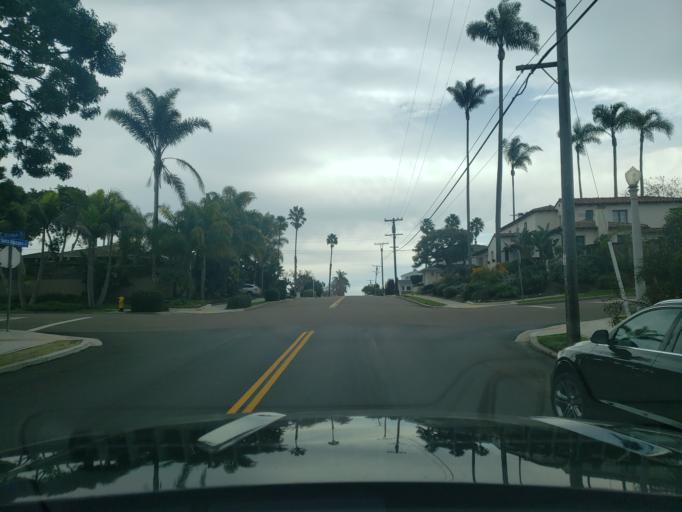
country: US
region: California
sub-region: San Diego County
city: Coronado
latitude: 32.7265
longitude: -117.2473
